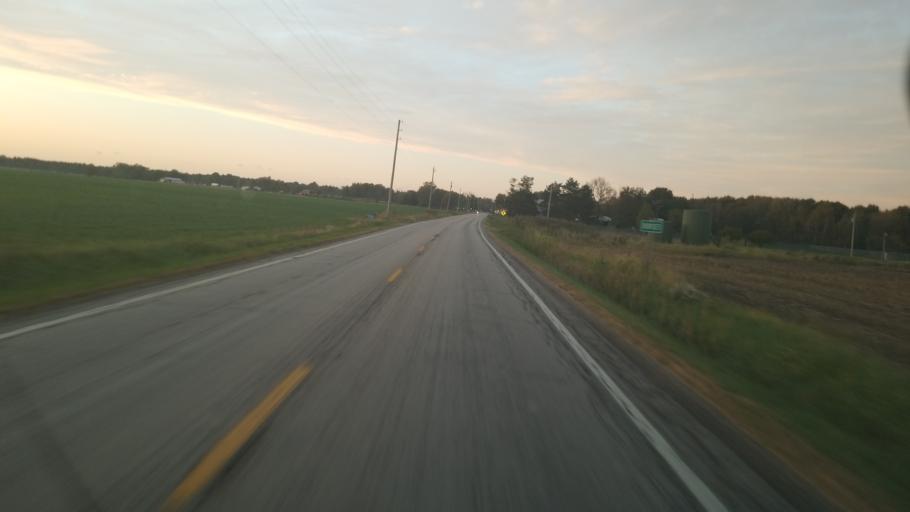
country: US
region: Ohio
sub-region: Ashtabula County
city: Andover
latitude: 41.6683
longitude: -80.6675
